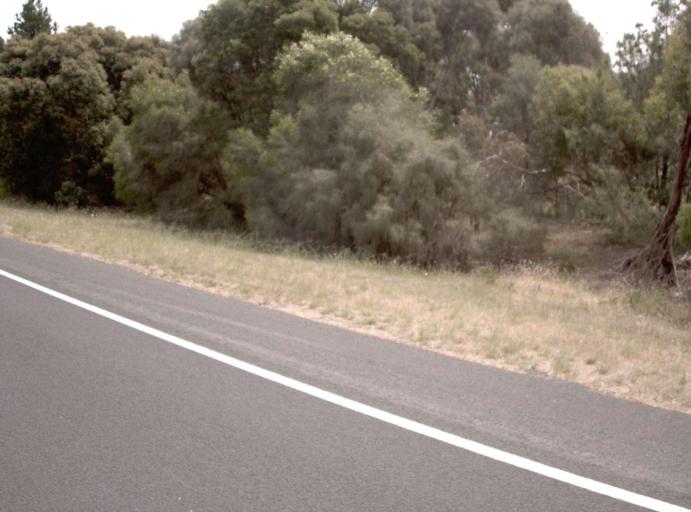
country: AU
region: Victoria
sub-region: Mornington Peninsula
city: Rosebud West
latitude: -38.3744
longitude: 144.8956
